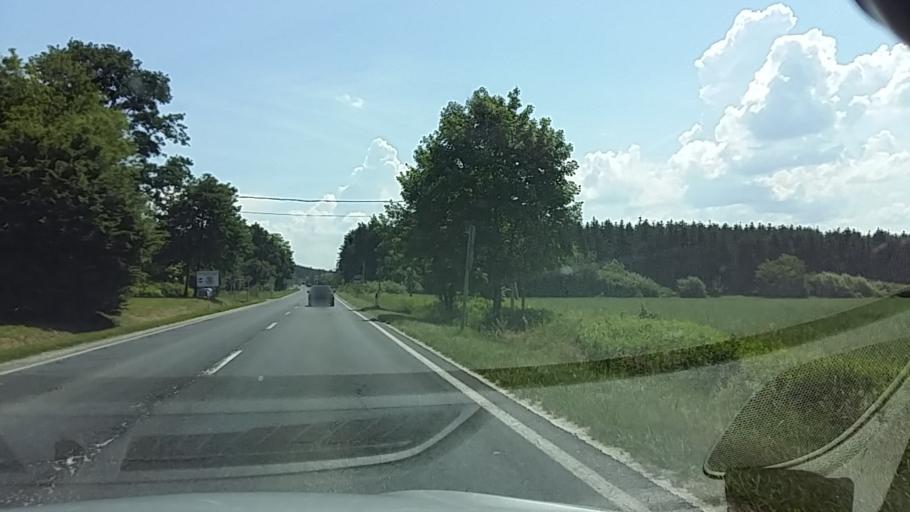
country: AT
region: Burgenland
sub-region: Politischer Bezirk Gussing
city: Inzenhof
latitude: 46.9796
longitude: 16.3196
